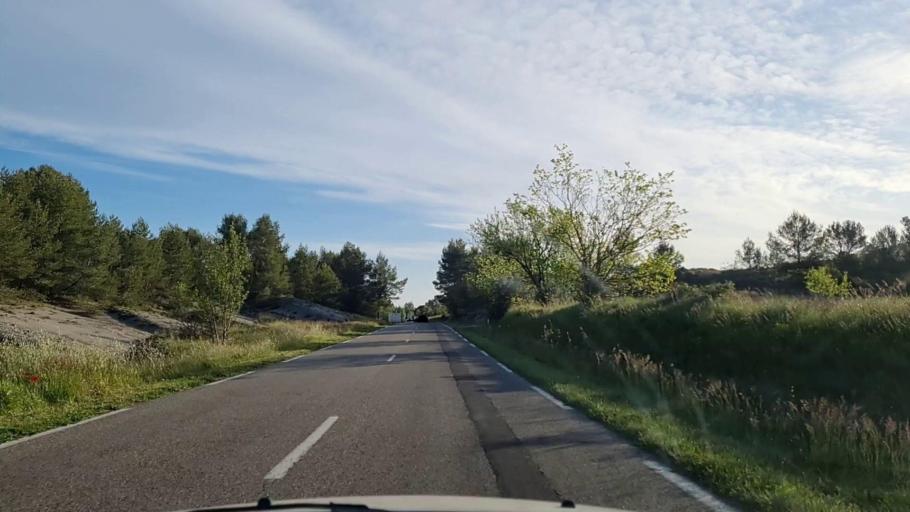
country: FR
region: Languedoc-Roussillon
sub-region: Departement du Gard
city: Ledignan
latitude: 43.9090
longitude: 4.1078
